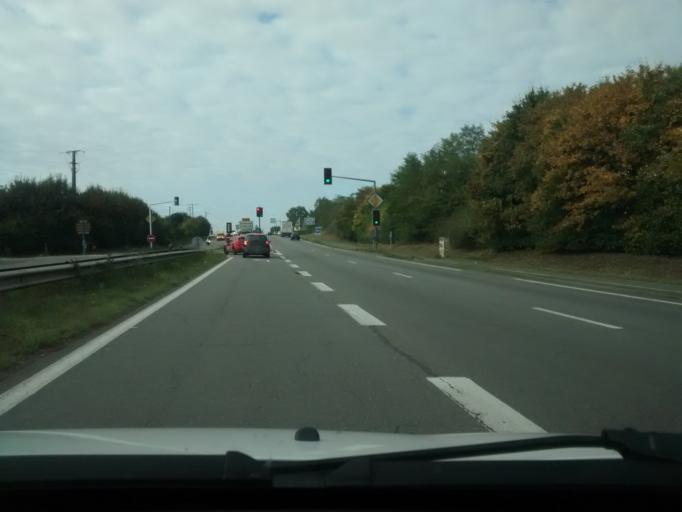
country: FR
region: Brittany
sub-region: Departement d'Ille-et-Vilaine
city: Vezin-le-Coquet
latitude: 48.1021
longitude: -1.7532
